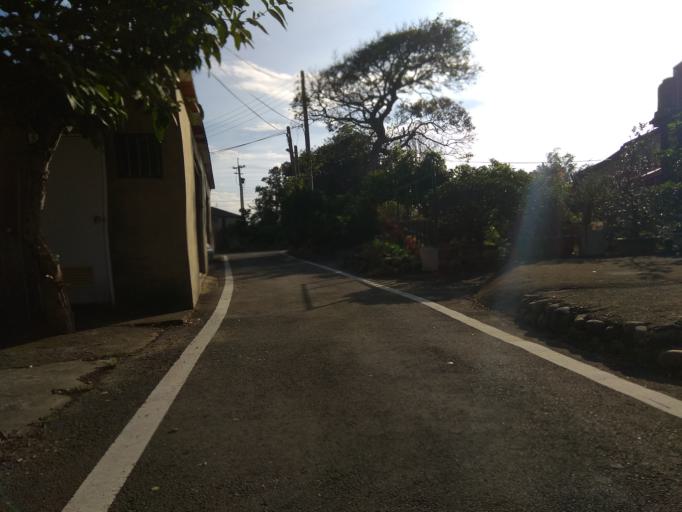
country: TW
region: Taiwan
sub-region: Hsinchu
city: Zhubei
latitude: 24.9820
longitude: 121.0585
